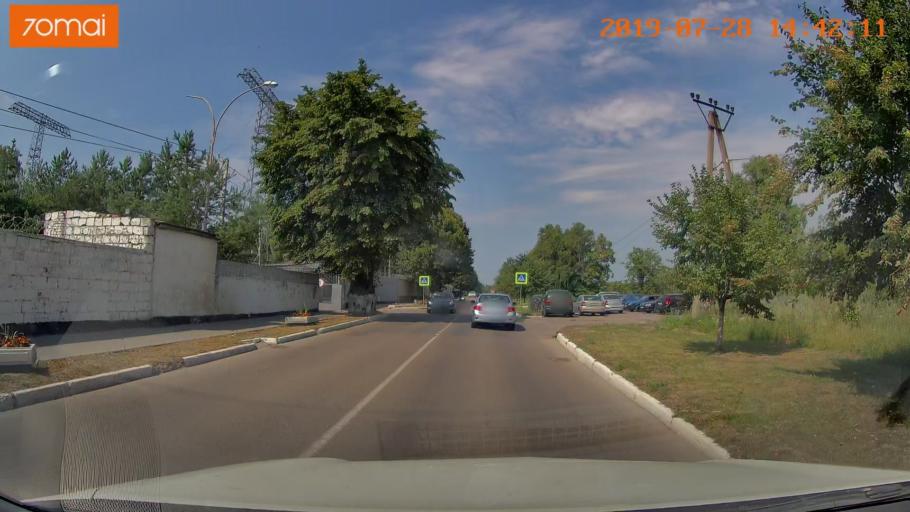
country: RU
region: Kaliningrad
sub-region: Gorod Kaliningrad
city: Yantarnyy
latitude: 54.8585
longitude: 19.9431
